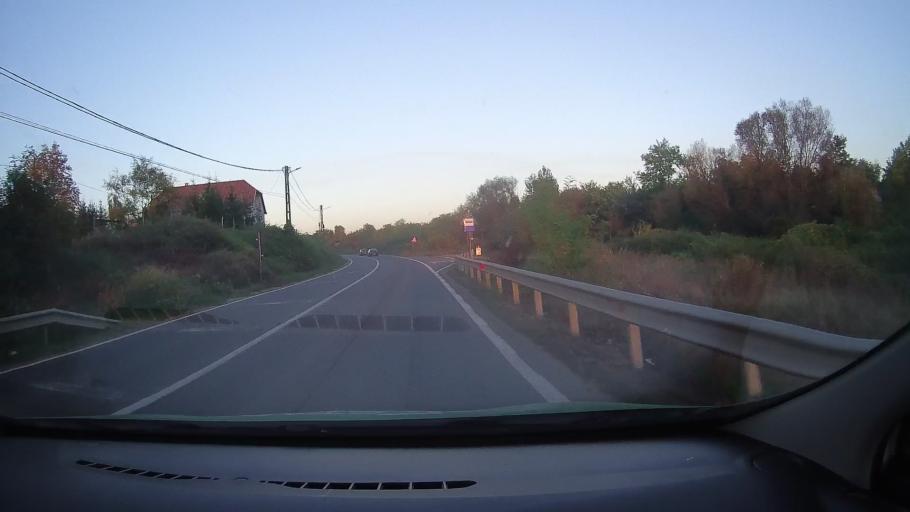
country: RO
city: Szekelyhid
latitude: 47.3605
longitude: 22.1117
